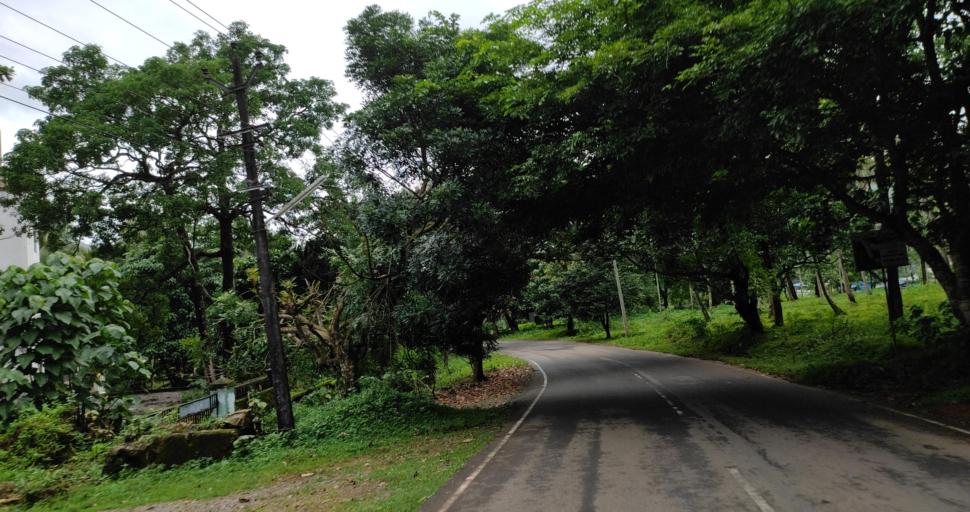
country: IN
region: Kerala
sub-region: Ernakulam
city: Angamali
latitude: 10.2890
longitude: 76.5593
